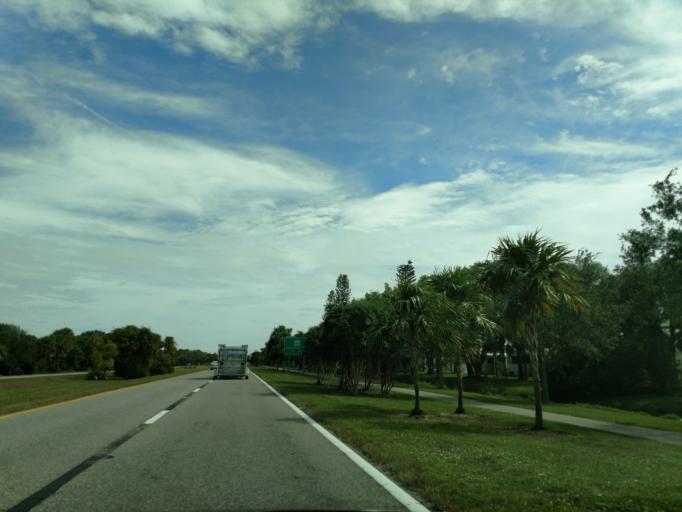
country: US
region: Florida
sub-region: Lee County
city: Iona
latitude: 26.4940
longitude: -81.9569
